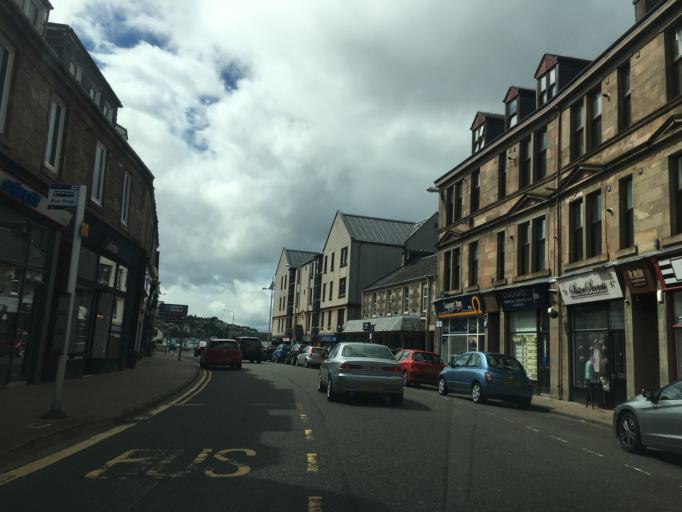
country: GB
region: Scotland
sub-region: Inverclyde
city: Gourock
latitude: 55.9617
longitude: -4.8200
